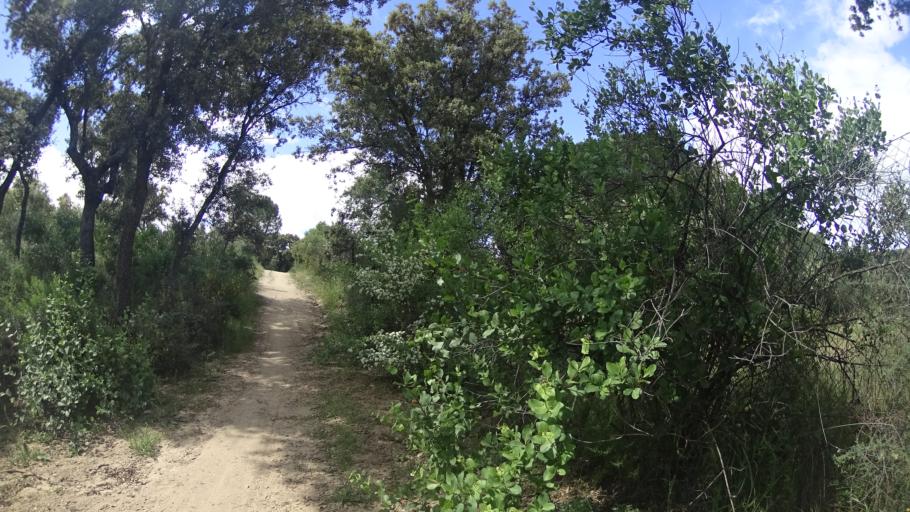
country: ES
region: Madrid
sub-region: Provincia de Madrid
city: Villaviciosa de Odon
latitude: 40.3895
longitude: -3.9399
